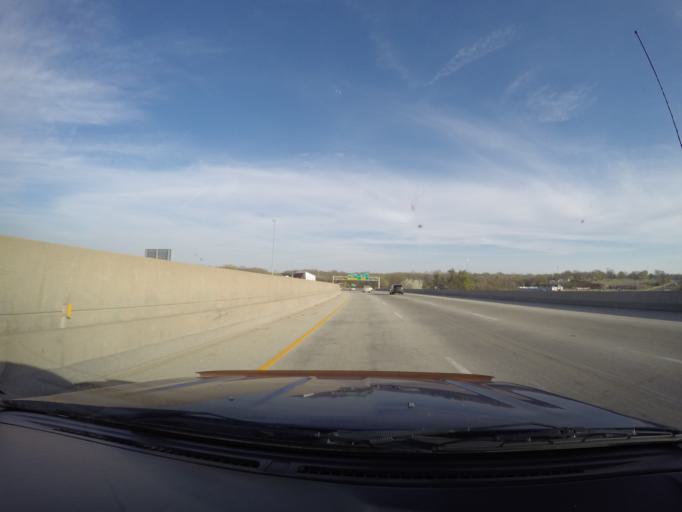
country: US
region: Kansas
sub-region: Shawnee County
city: Topeka
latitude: 39.0402
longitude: -95.6691
